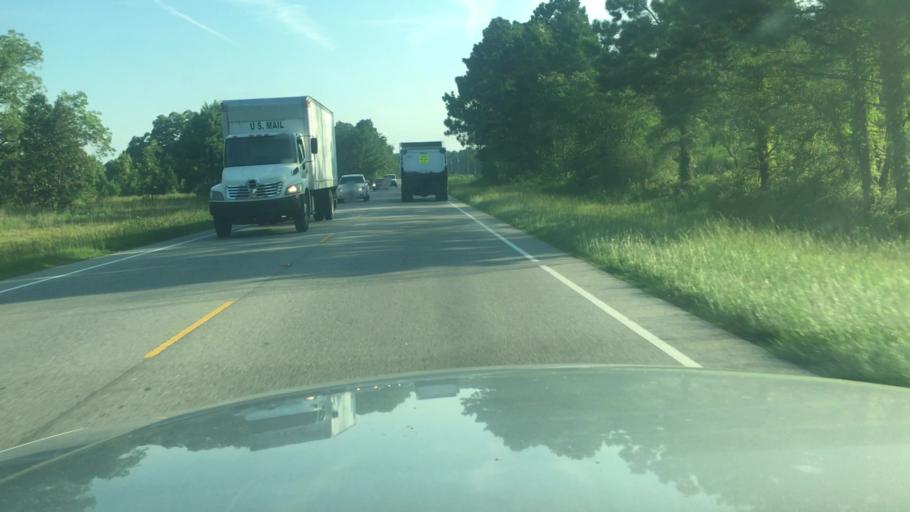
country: US
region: North Carolina
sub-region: Cumberland County
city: Eastover
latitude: 35.1882
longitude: -78.8517
